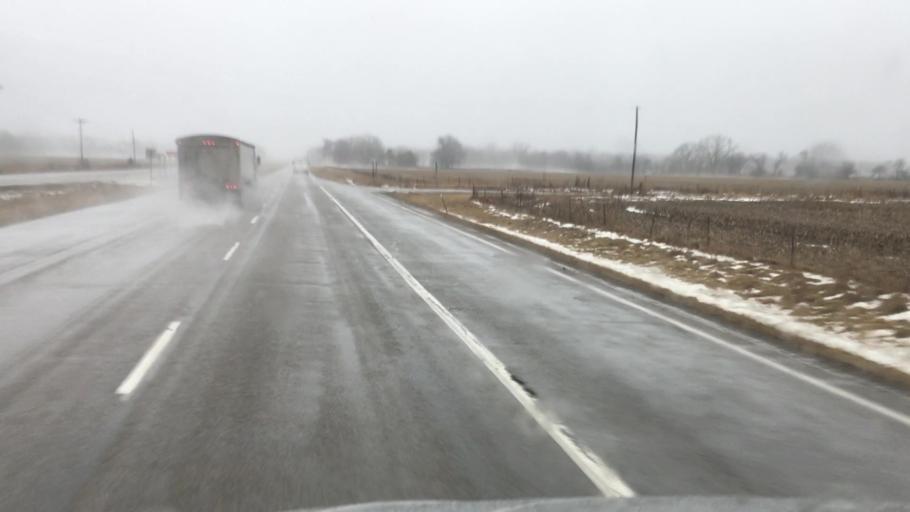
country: US
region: Indiana
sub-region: Newton County
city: Roselawn
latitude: 41.1165
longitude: -87.4489
